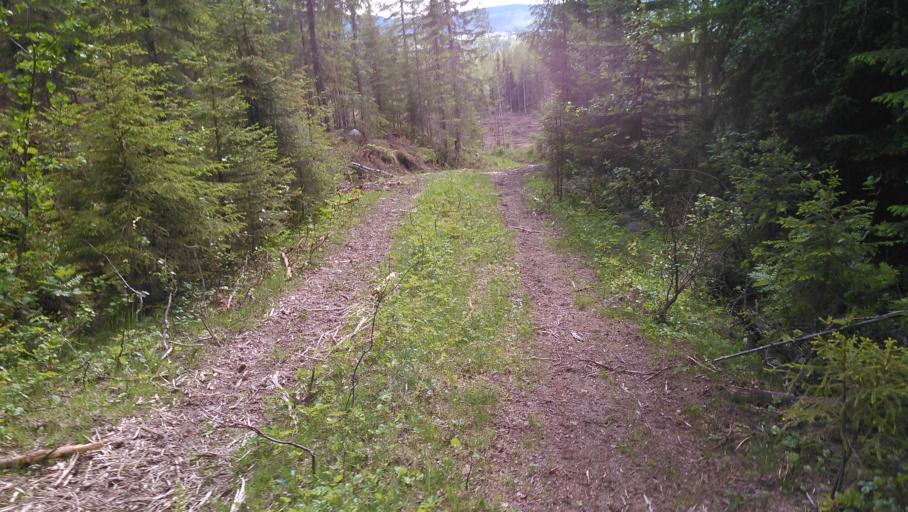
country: SE
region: Vaesterbotten
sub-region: Vannas Kommun
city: Vannasby
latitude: 63.9302
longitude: 19.8927
